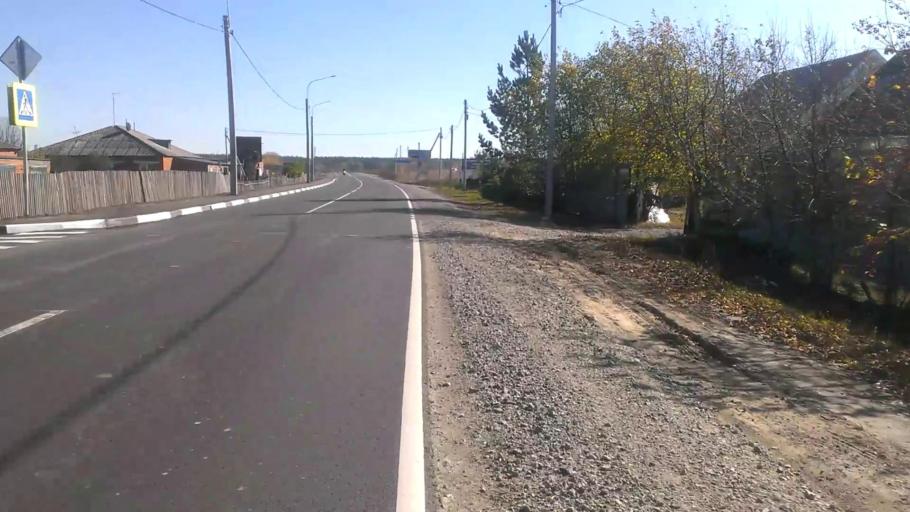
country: RU
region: Altai Krai
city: Sannikovo
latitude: 53.3148
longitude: 83.9603
